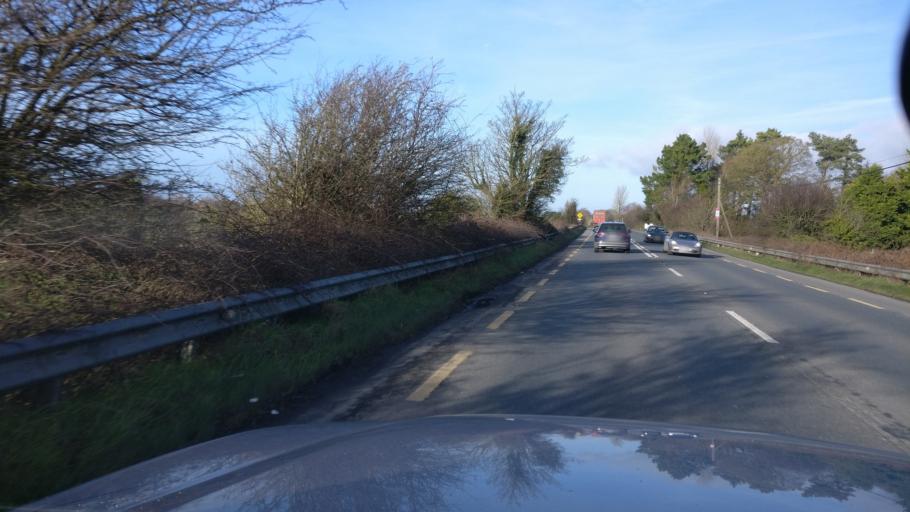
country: IE
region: Leinster
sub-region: Uibh Fhaili
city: Tullamore
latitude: 53.2441
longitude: -7.4777
